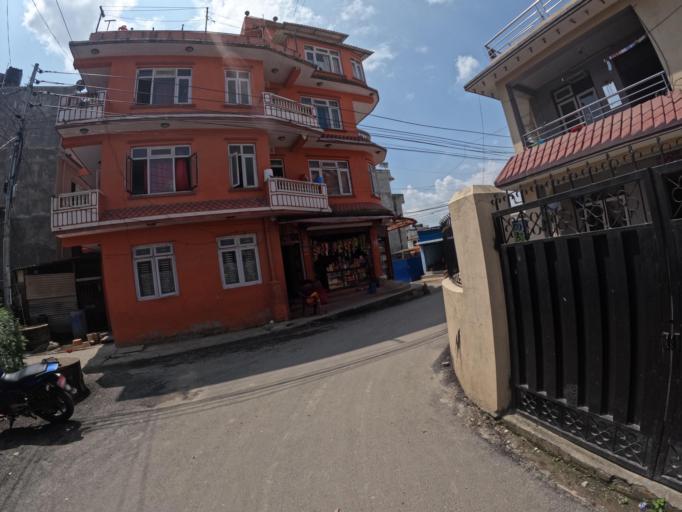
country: NP
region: Central Region
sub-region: Bagmati Zone
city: Bhaktapur
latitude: 27.6729
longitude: 85.3748
